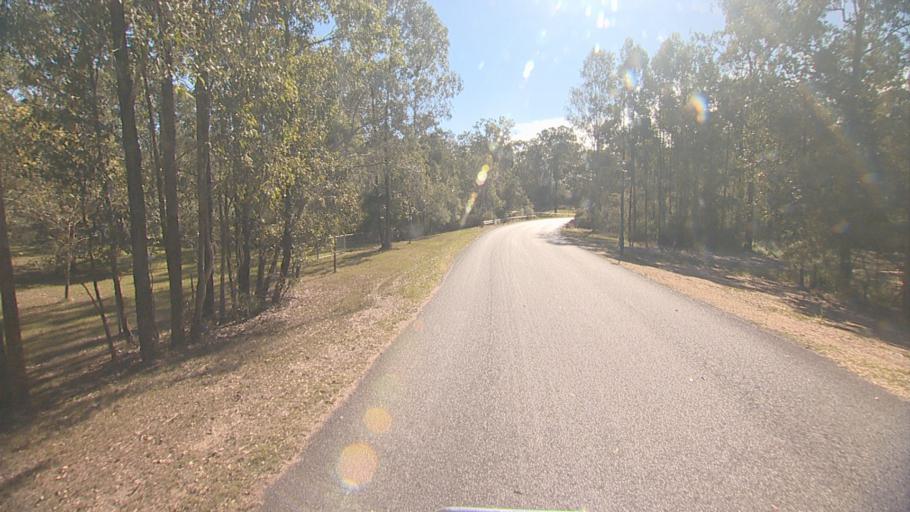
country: AU
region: Queensland
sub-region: Ipswich
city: Springfield Lakes
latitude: -27.7155
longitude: 152.9309
